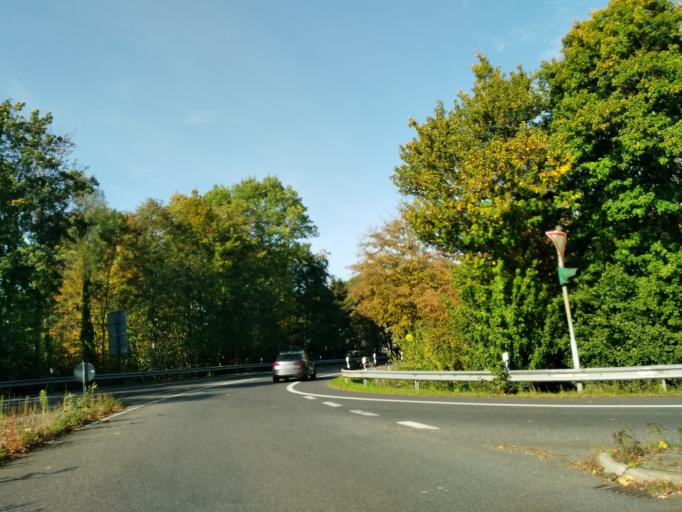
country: DE
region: North Rhine-Westphalia
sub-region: Regierungsbezirk Koln
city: Hennef
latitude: 50.7031
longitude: 7.2883
